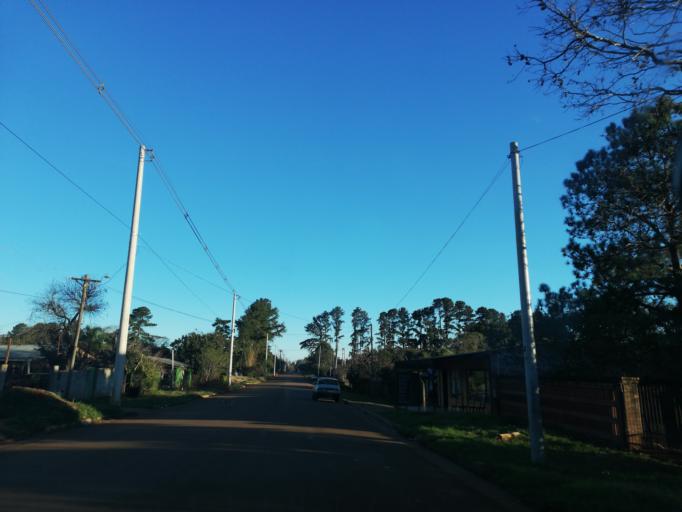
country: AR
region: Misiones
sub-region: Departamento de Candelaria
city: Candelaria
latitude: -27.4640
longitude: -55.7490
